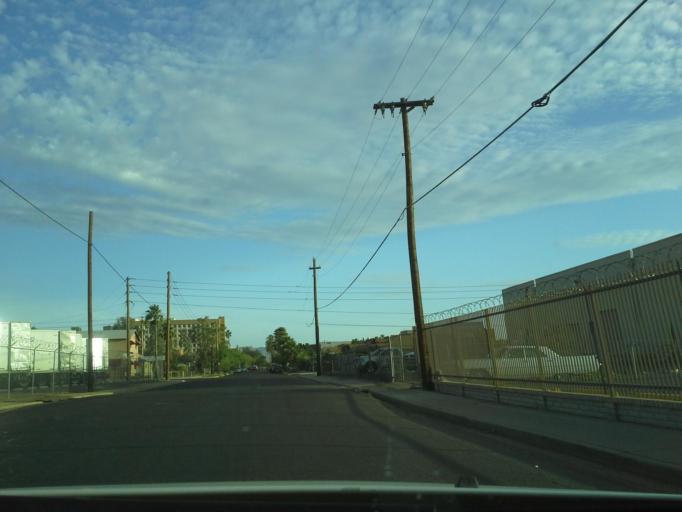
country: US
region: Arizona
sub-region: Maricopa County
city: Phoenix
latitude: 33.4558
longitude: -112.0957
